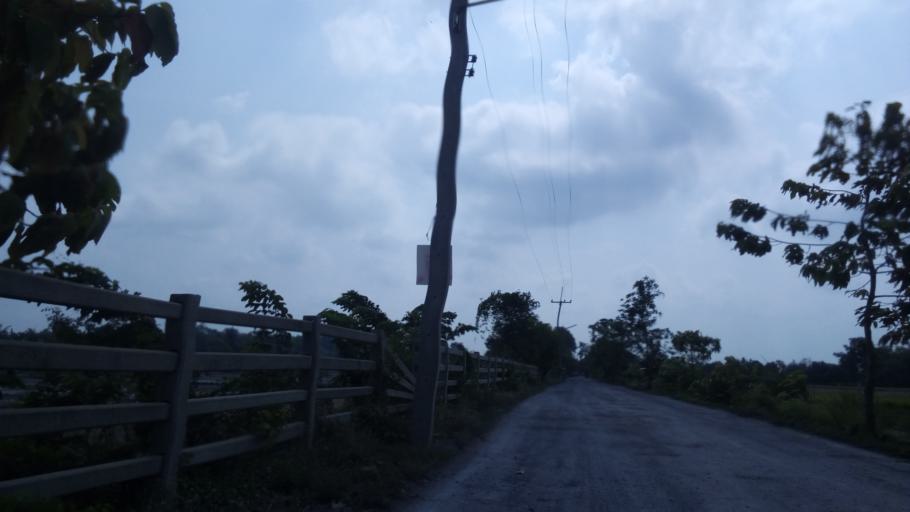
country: TH
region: Pathum Thani
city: Nong Suea
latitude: 14.1886
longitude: 100.8425
